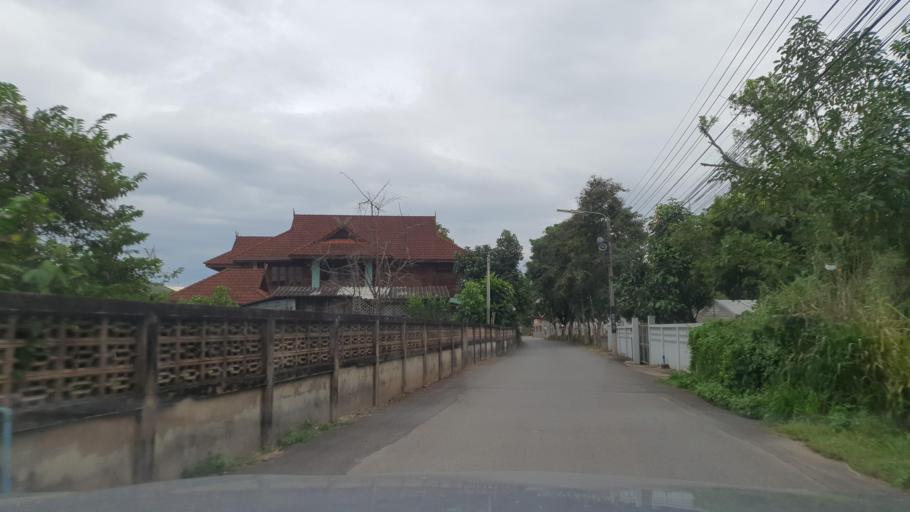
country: TH
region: Chiang Mai
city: San Sai
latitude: 18.9236
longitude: 98.9416
